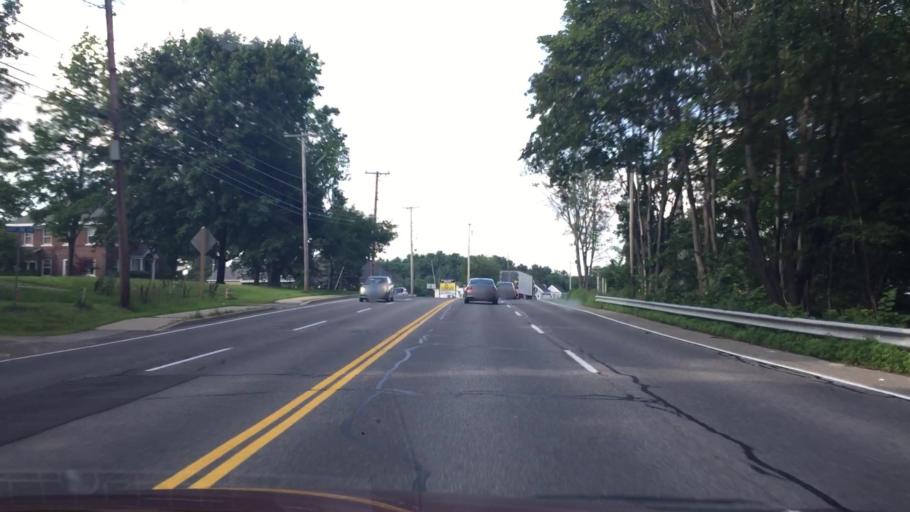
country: US
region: Maine
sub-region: Cumberland County
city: West Scarborough
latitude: 43.5617
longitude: -70.3987
